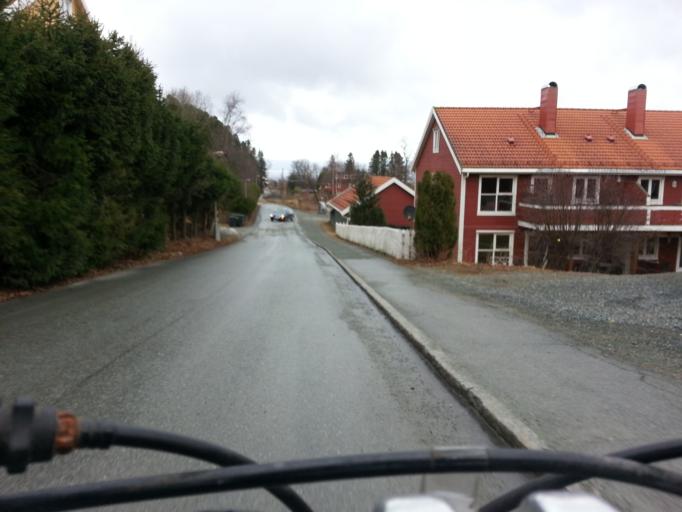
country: NO
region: Sor-Trondelag
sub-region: Trondheim
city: Trondheim
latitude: 63.4156
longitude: 10.3759
